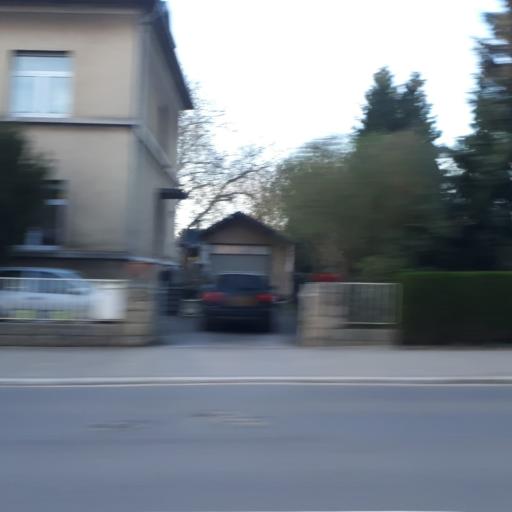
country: LU
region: Luxembourg
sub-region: Canton de Luxembourg
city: Strassen
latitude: 49.6177
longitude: 6.0897
